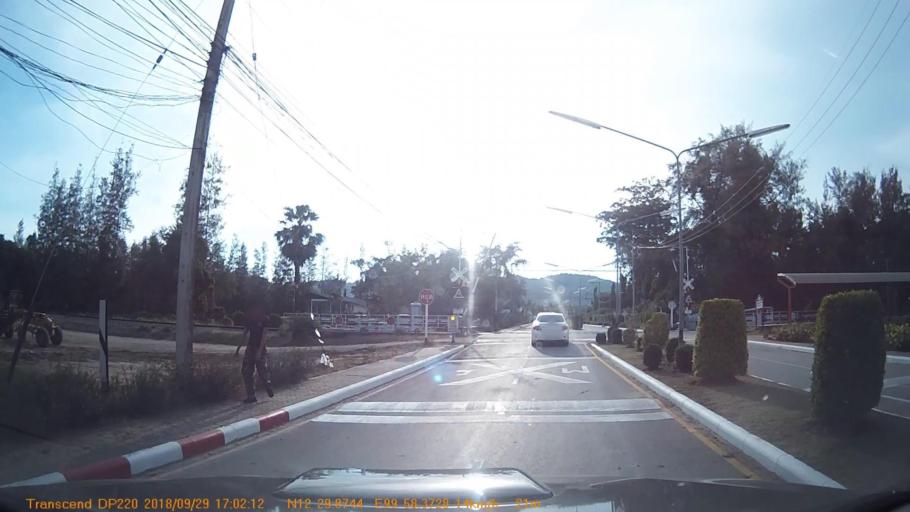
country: TH
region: Prachuap Khiri Khan
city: Hua Hin
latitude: 12.4980
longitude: 99.9726
